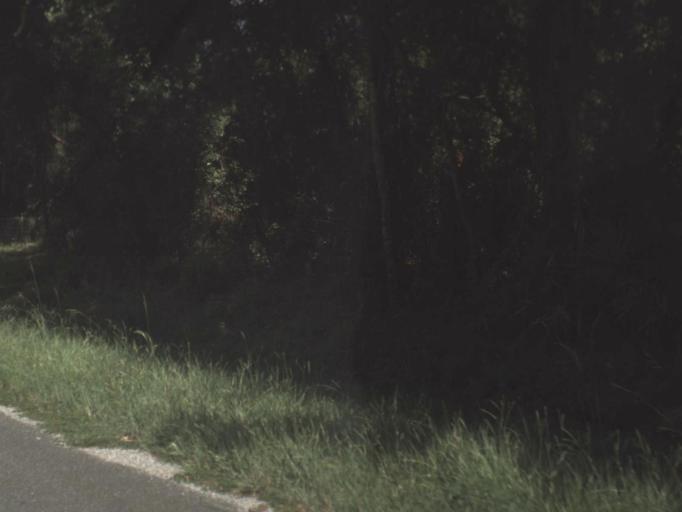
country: US
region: Florida
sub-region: Clay County
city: Green Cove Springs
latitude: 29.9892
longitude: -81.5762
